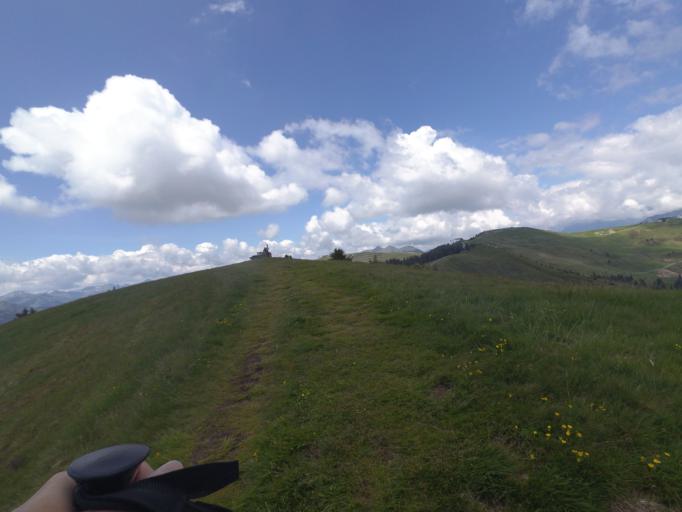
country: AT
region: Salzburg
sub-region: Politischer Bezirk Zell am See
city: Viehhofen
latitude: 47.3926
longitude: 12.7110
